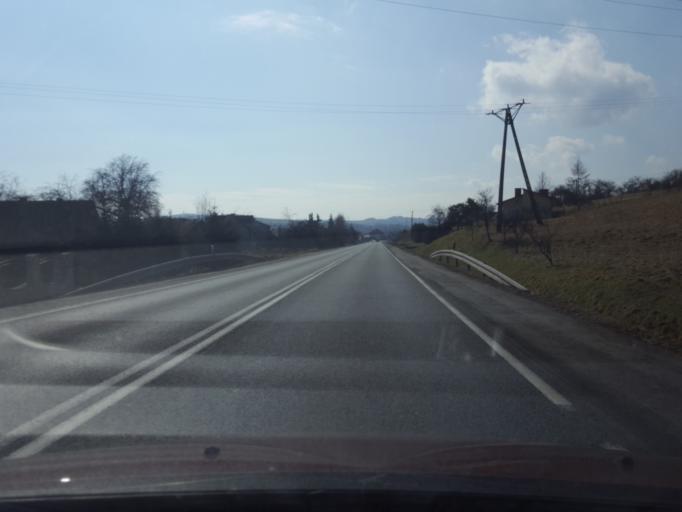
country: PL
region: Lesser Poland Voivodeship
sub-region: Powiat nowosadecki
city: Lososina Dolna
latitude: 49.7611
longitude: 20.6343
